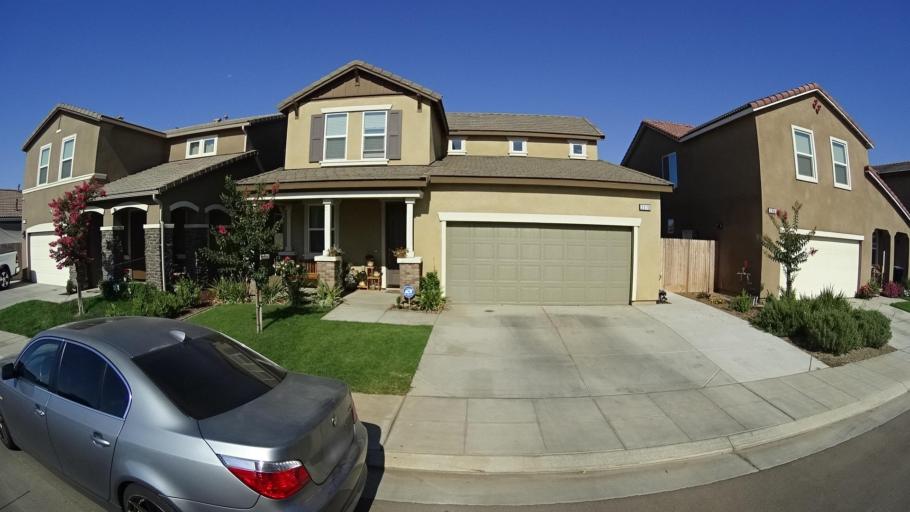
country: US
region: California
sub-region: Fresno County
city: Sunnyside
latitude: 36.7157
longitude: -119.7338
